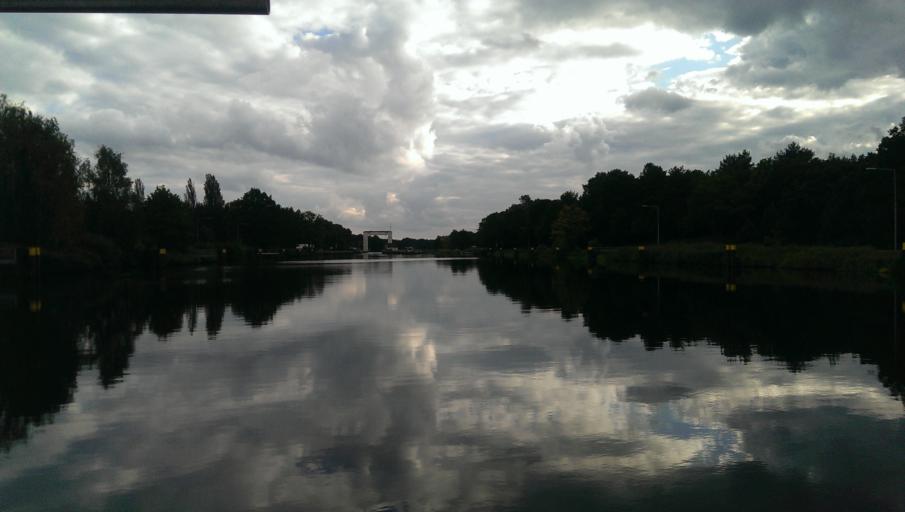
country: DE
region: Brandenburg
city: Oranienburg
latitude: 52.7729
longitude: 13.2801
